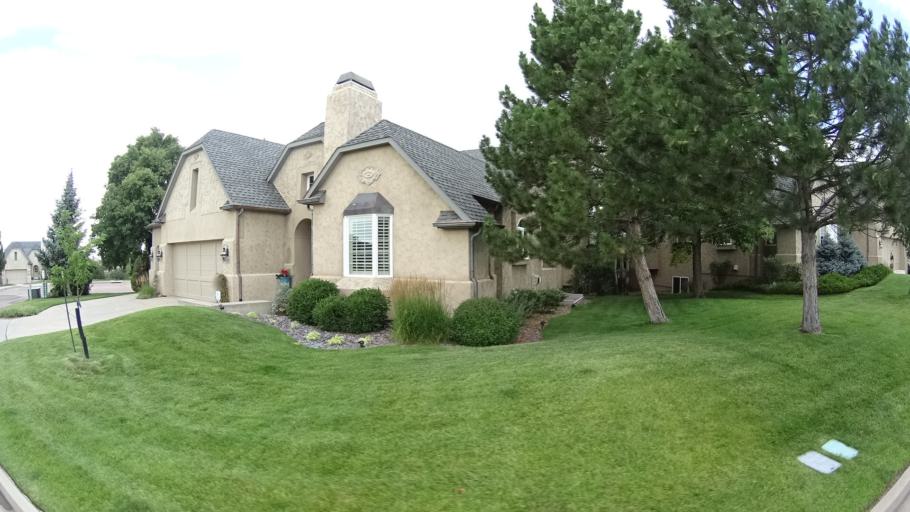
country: US
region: Colorado
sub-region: El Paso County
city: Colorado Springs
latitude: 38.9078
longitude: -104.8296
